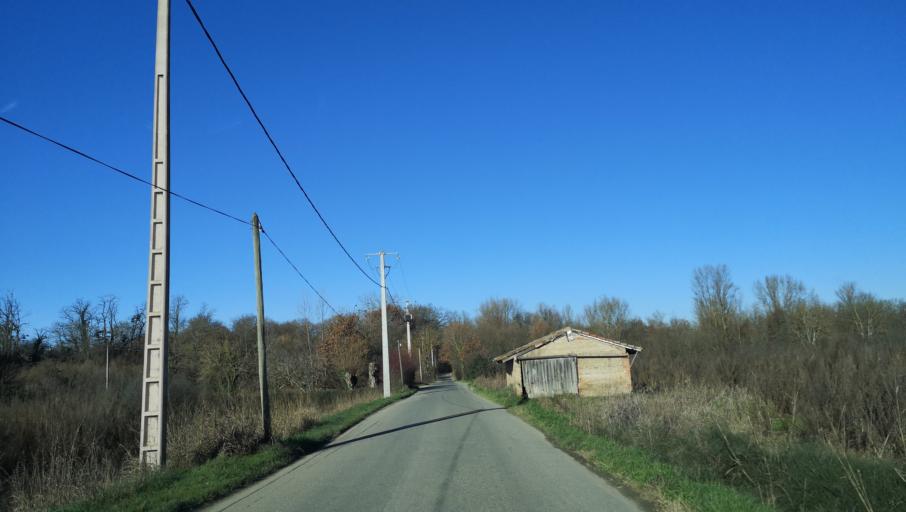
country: FR
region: Midi-Pyrenees
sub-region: Departement de la Haute-Garonne
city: Beauzelle
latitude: 43.6593
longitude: 1.3947
